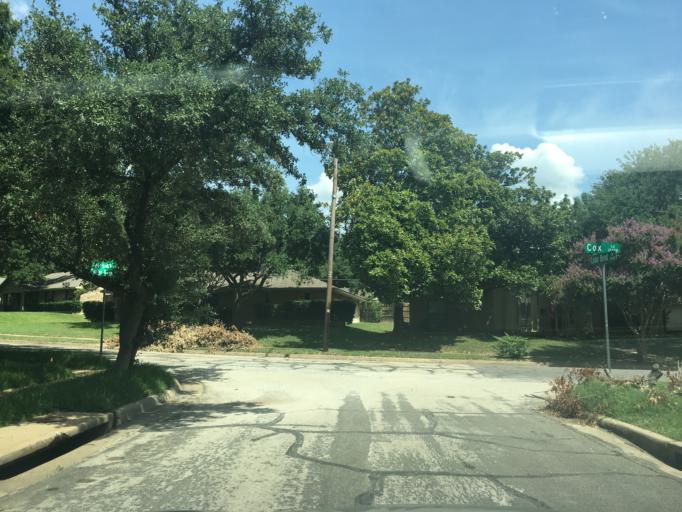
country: US
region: Texas
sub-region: Dallas County
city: Farmers Branch
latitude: 32.9177
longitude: -96.8509
